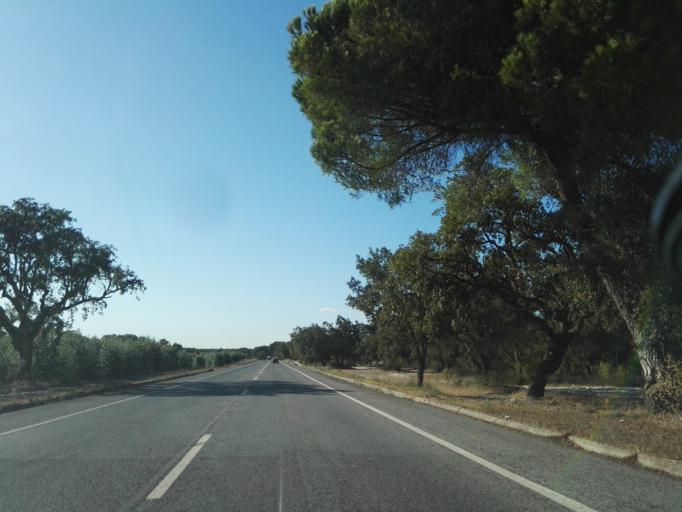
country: PT
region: Santarem
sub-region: Benavente
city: Poceirao
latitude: 38.8701
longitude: -8.7964
